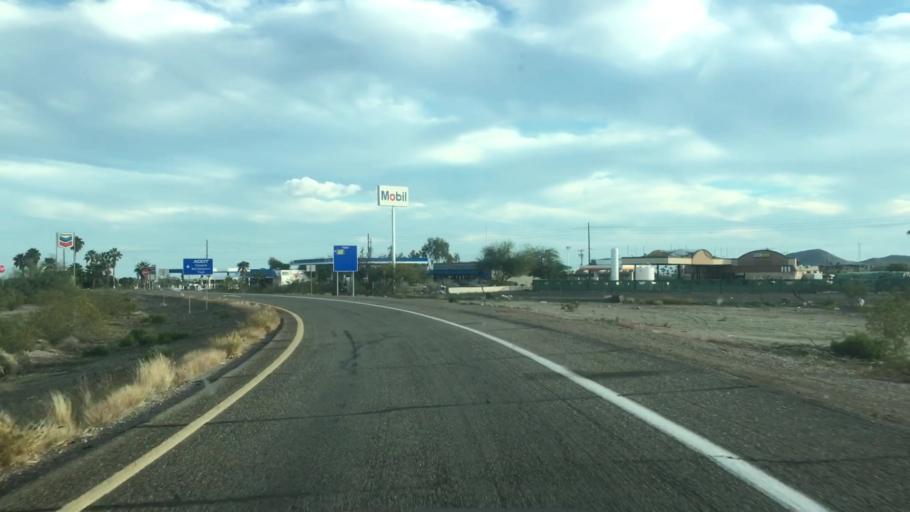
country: US
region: Arizona
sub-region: Maricopa County
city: Buckeye
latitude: 33.4960
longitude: -112.9385
